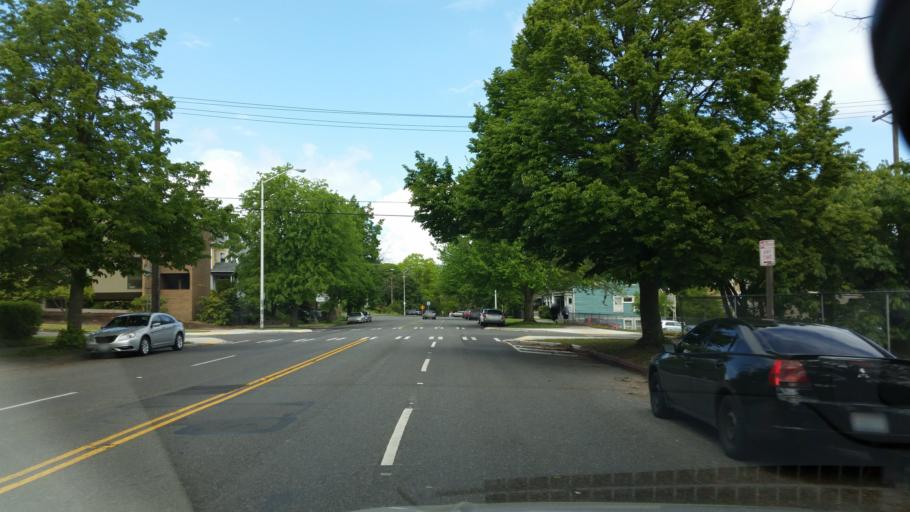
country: US
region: Washington
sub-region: Pierce County
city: Tacoma
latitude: 47.2550
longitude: -122.4480
